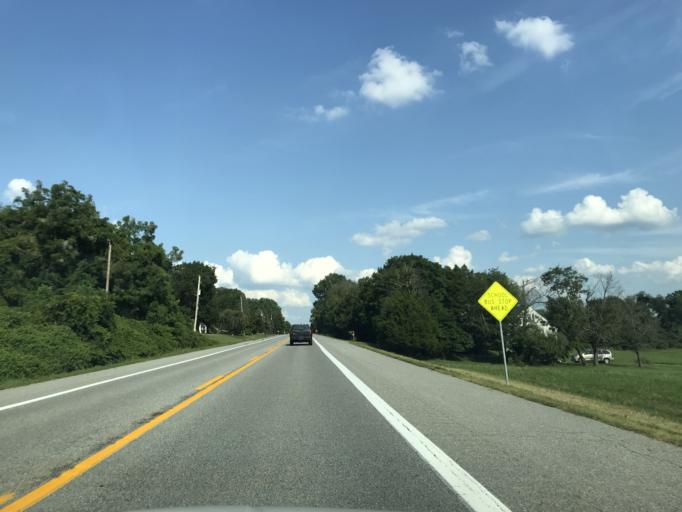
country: US
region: Maryland
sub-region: Cecil County
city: Elkton
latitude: 39.6998
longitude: -75.8486
